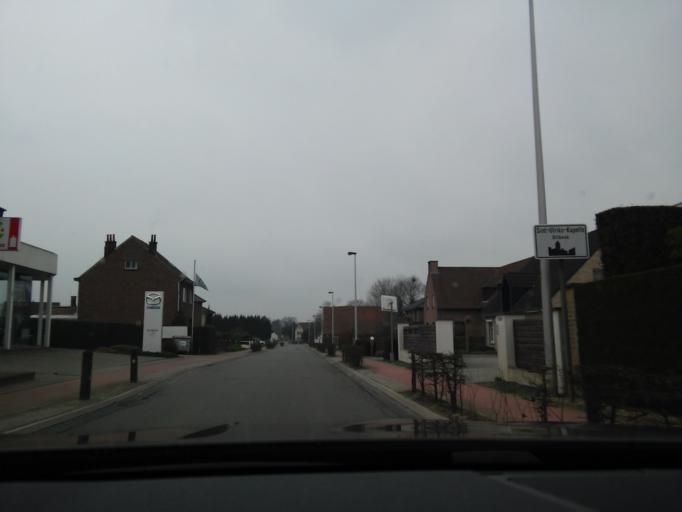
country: BE
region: Flanders
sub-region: Provincie Vlaams-Brabant
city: Asse
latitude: 50.8798
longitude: 4.2282
